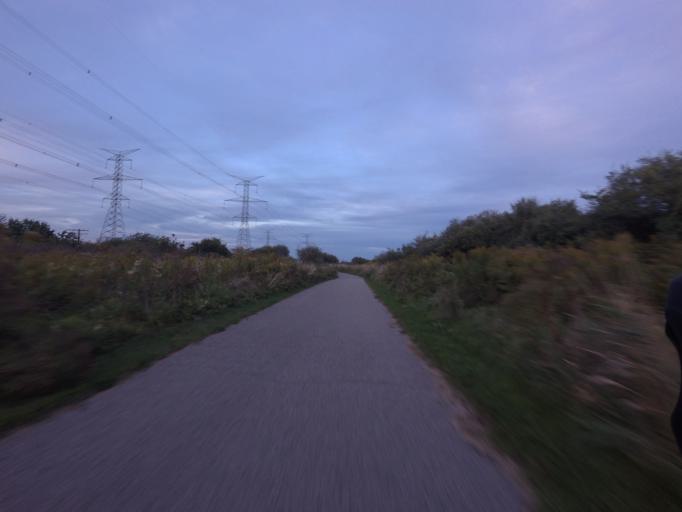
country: CA
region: Ontario
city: Oshawa
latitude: 43.8983
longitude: -78.6329
